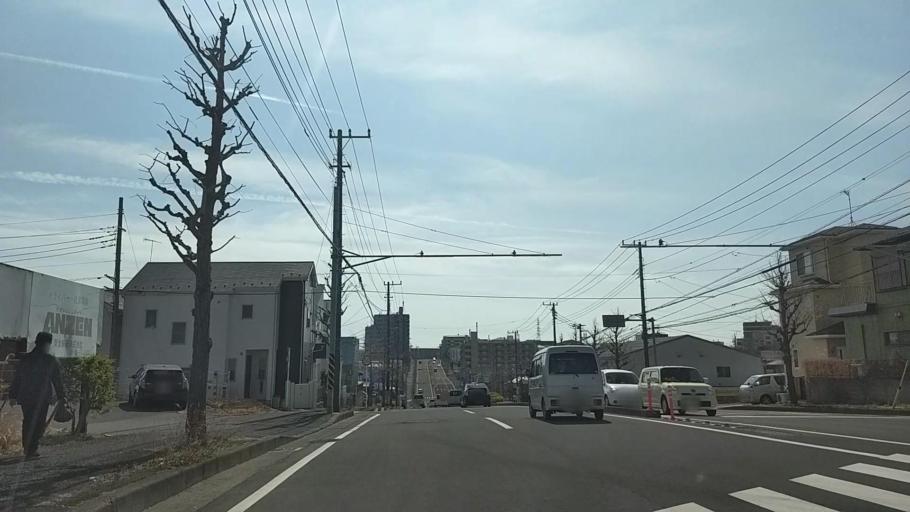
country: JP
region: Kanagawa
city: Fujisawa
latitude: 35.3831
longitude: 139.4563
